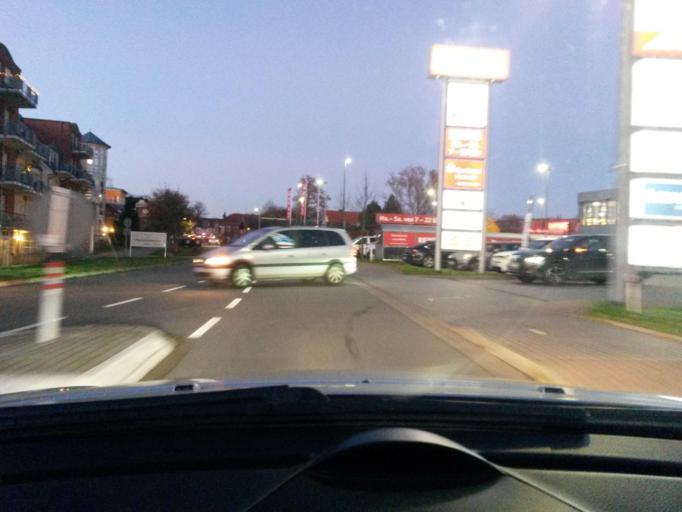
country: DE
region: Schleswig-Holstein
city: Barsbuettel
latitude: 53.5671
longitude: 10.1635
